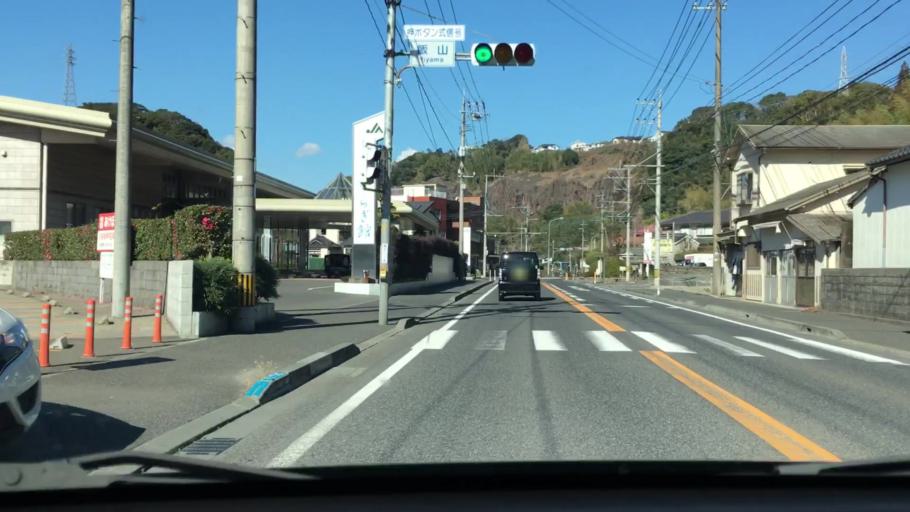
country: JP
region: Kagoshima
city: Kagoshima-shi
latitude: 31.6304
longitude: 130.5245
